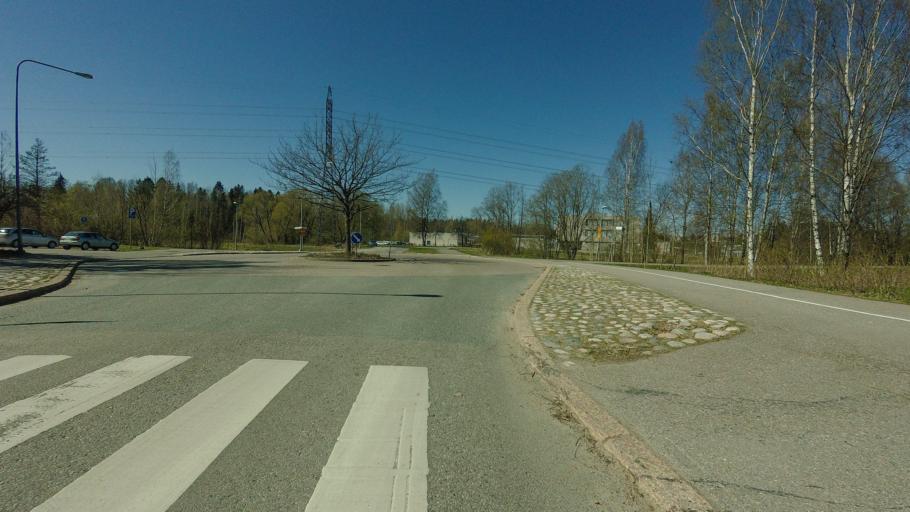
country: FI
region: Uusimaa
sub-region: Helsinki
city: Vantaa
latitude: 60.2137
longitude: 25.0752
